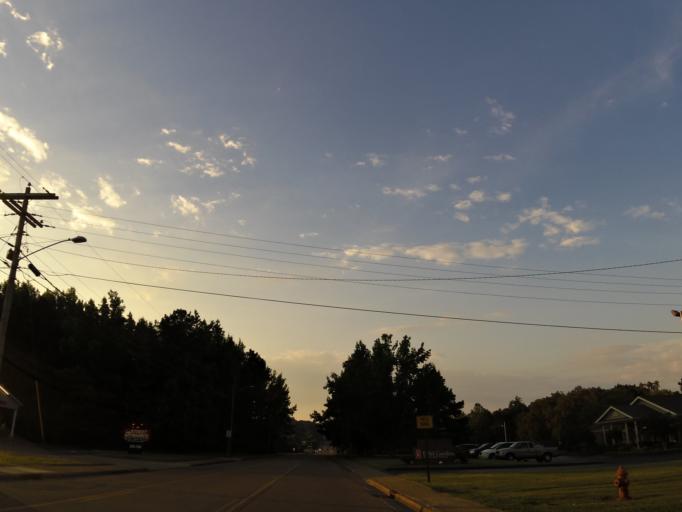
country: US
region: Tennessee
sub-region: Henry County
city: Paris
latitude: 36.2854
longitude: -88.3033
